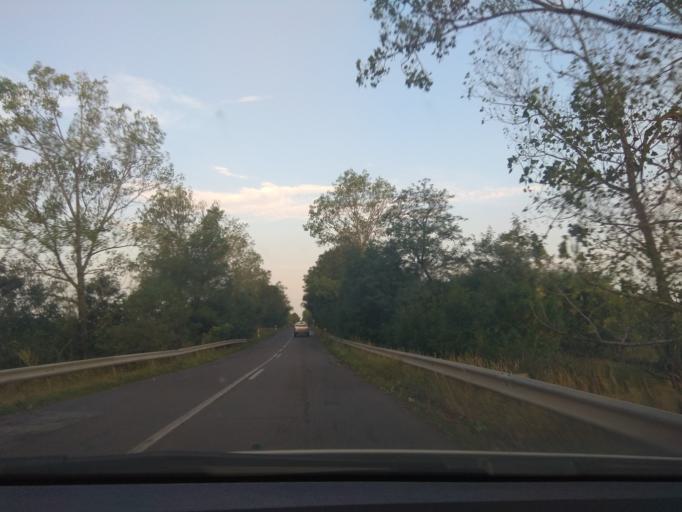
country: HU
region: Heves
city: Andornaktalya
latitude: 47.8314
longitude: 20.4471
